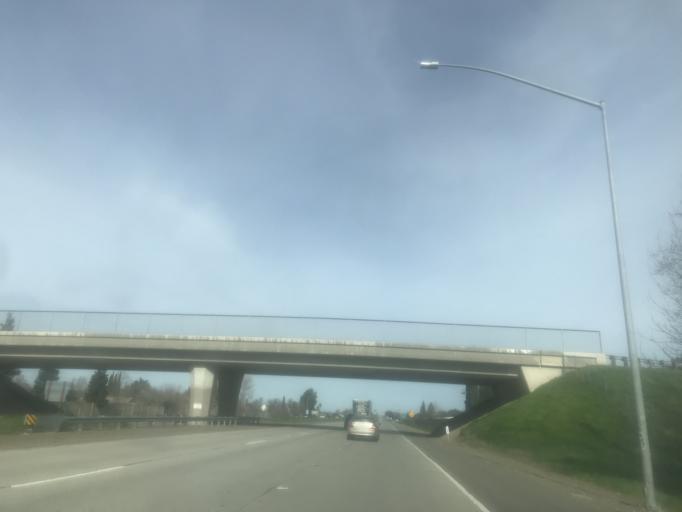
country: US
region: California
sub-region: Yolo County
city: Woodland
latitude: 38.6677
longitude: -121.7511
